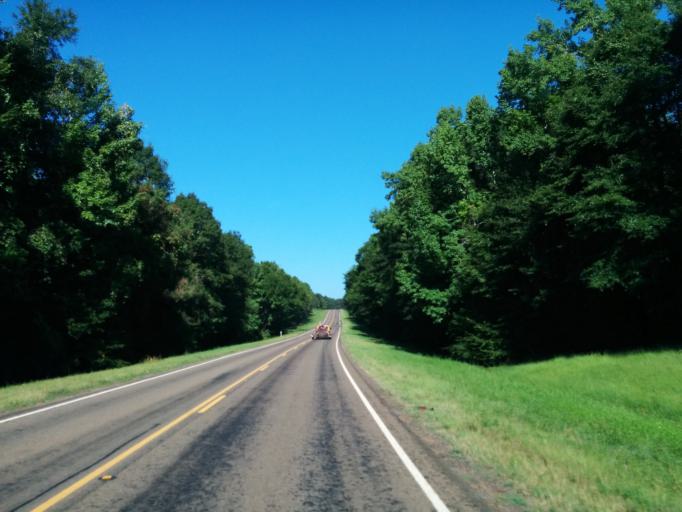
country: US
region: Texas
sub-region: Sabine County
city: Milam
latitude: 31.4292
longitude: -93.8017
